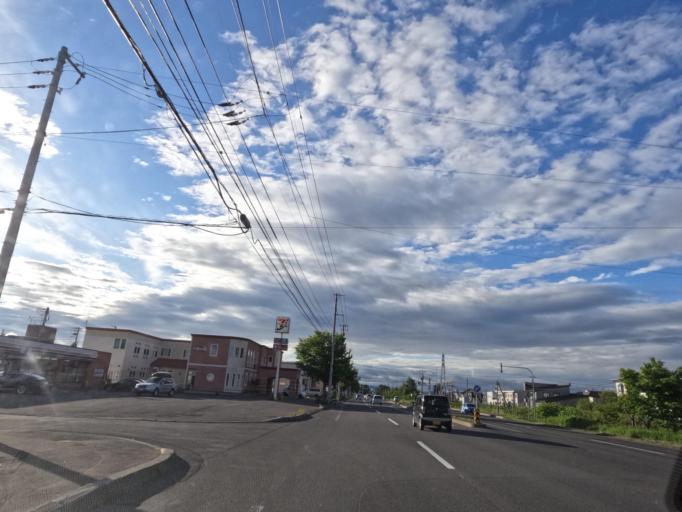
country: JP
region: Hokkaido
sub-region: Asahikawa-shi
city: Asahikawa
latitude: 43.7385
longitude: 142.3609
